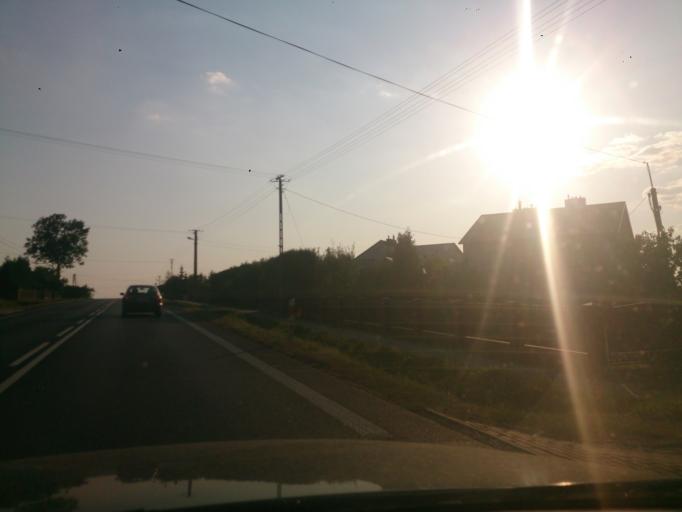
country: PL
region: Subcarpathian Voivodeship
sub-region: Powiat kolbuszowski
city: Majdan Krolewski
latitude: 50.3850
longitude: 21.7535
